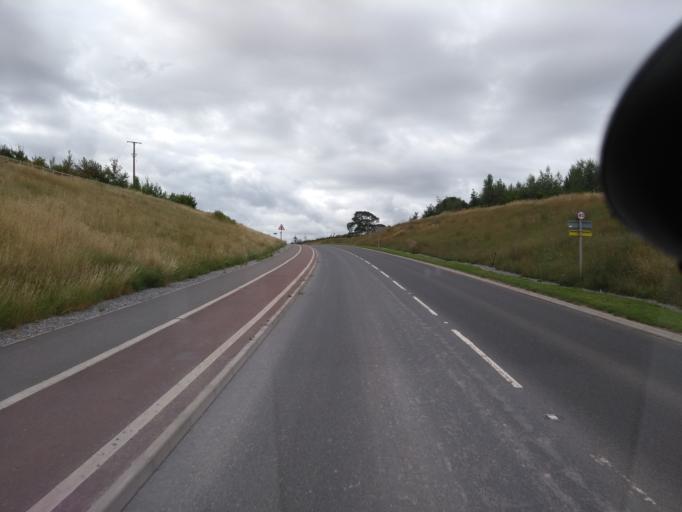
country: GB
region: England
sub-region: Somerset
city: Bridgwater
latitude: 51.1555
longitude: -3.0714
